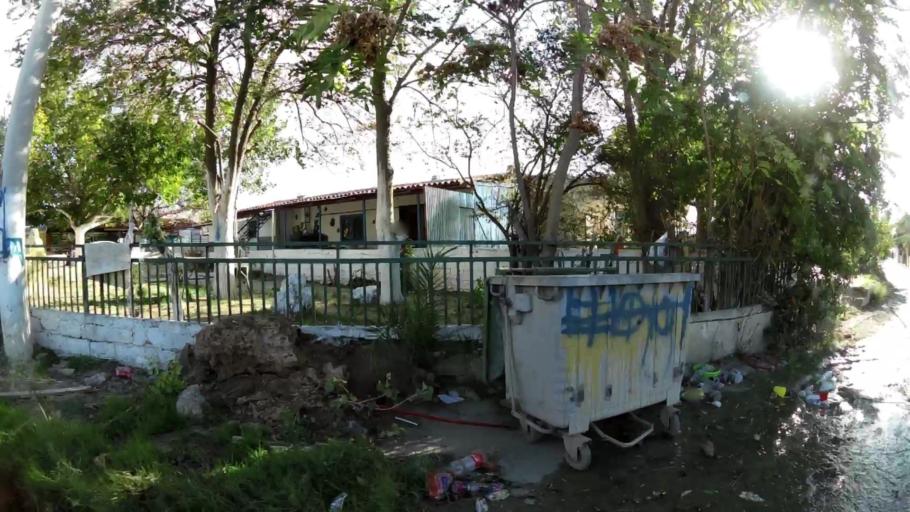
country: GR
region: Attica
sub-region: Nomarchia Anatolikis Attikis
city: Acharnes
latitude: 38.0756
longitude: 23.7485
